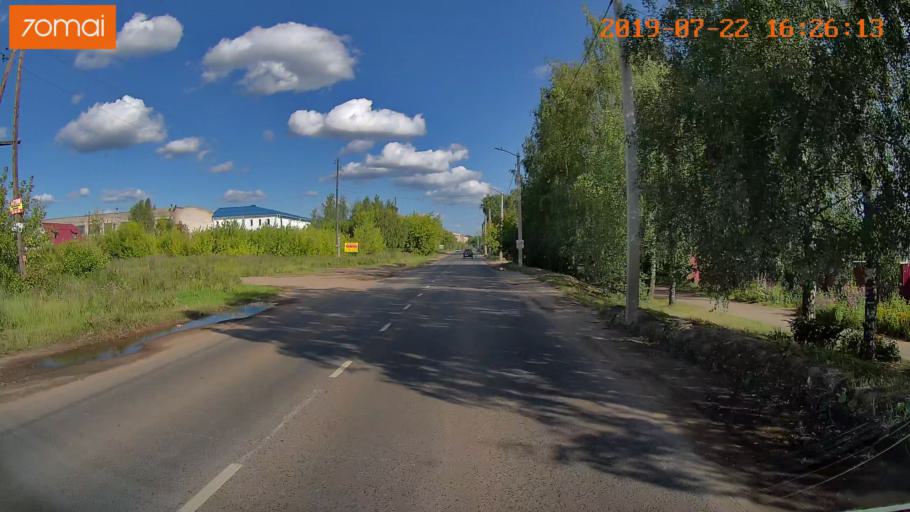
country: RU
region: Ivanovo
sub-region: Gorod Ivanovo
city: Ivanovo
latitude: 57.0501
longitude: 40.9315
